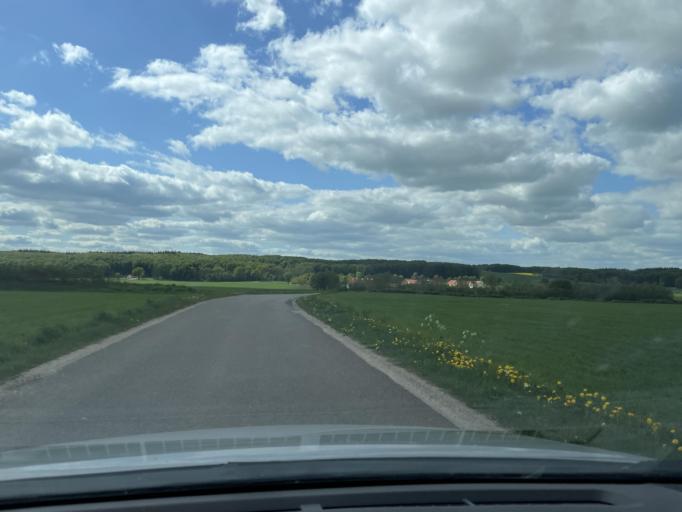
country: DK
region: Central Jutland
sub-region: Odder Kommune
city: Odder
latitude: 55.9099
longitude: 10.1166
